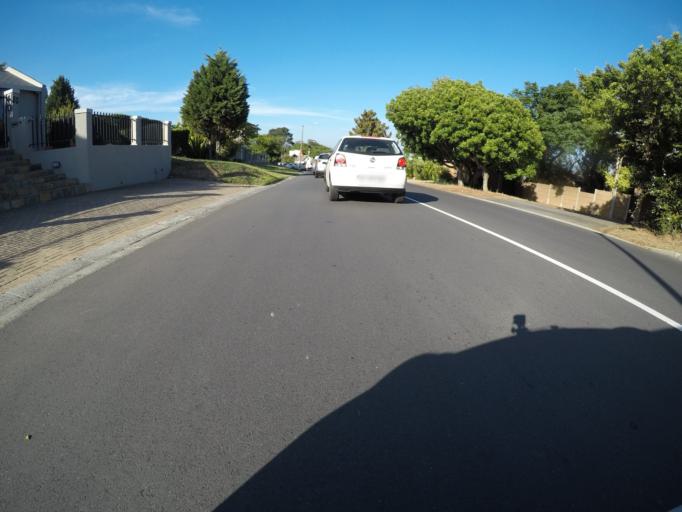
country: ZA
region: Western Cape
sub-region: City of Cape Town
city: Kraaifontein
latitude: -33.8735
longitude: 18.6474
